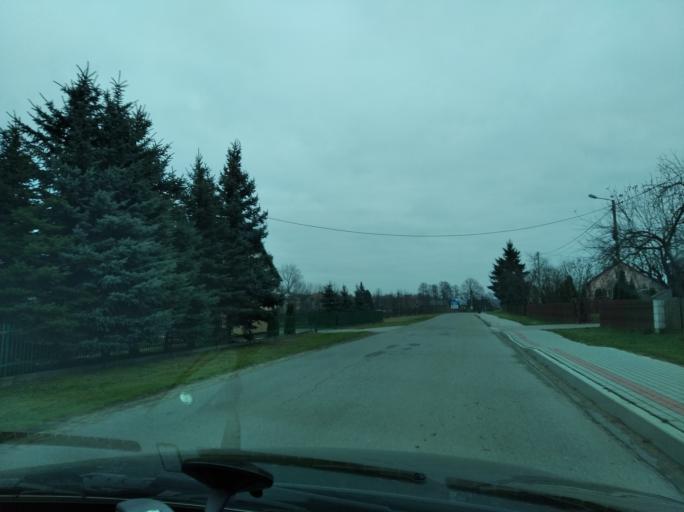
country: PL
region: Subcarpathian Voivodeship
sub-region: Powiat lancucki
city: Brzoza Stadnicka
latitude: 50.1963
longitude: 22.2716
